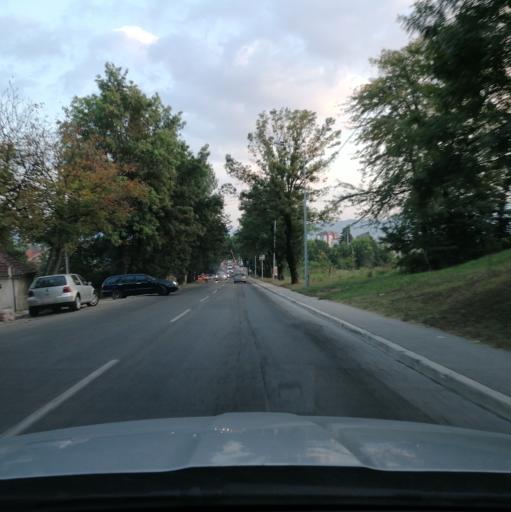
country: RS
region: Central Serbia
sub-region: Raski Okrug
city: Kraljevo
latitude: 43.7324
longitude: 20.6807
